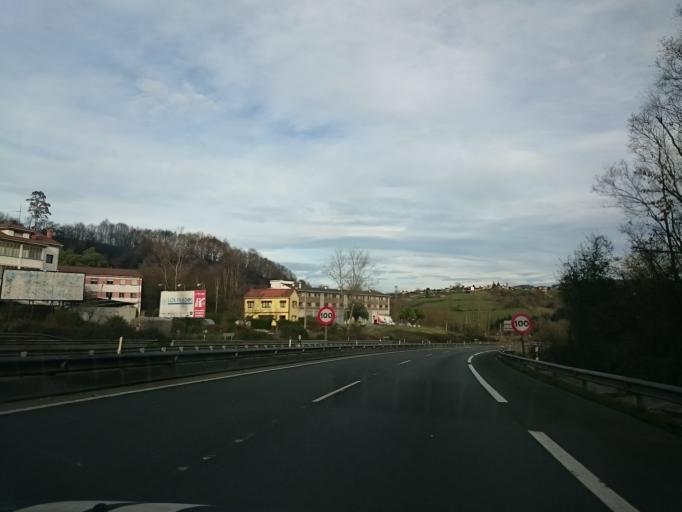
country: ES
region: Asturias
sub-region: Province of Asturias
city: Oviedo
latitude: 43.3263
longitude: -5.8755
